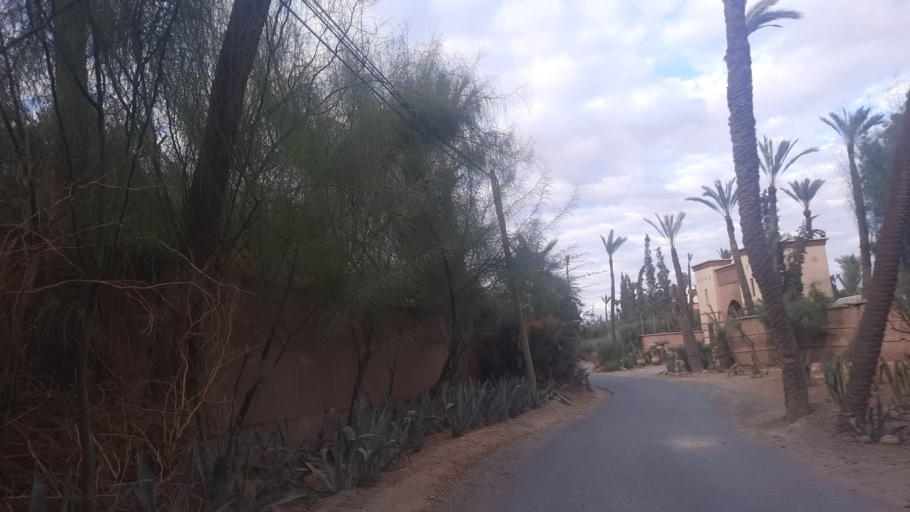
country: MA
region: Marrakech-Tensift-Al Haouz
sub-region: Marrakech
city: Marrakesh
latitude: 31.6739
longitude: -7.9534
